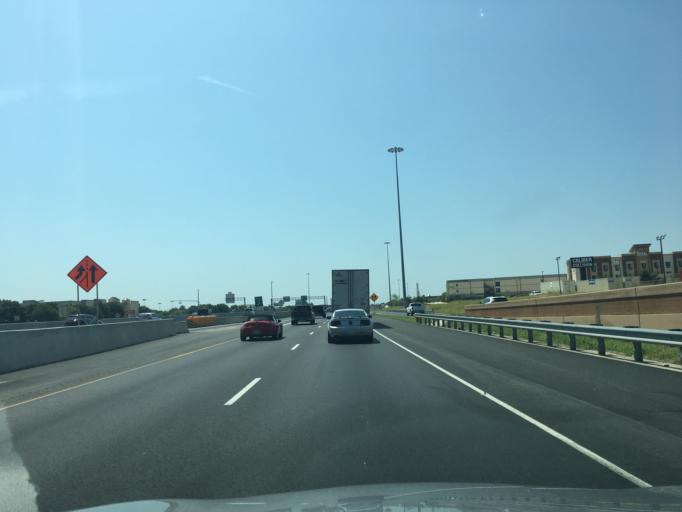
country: US
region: Texas
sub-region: Tarrant County
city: Blue Mound
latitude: 32.8571
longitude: -97.3140
